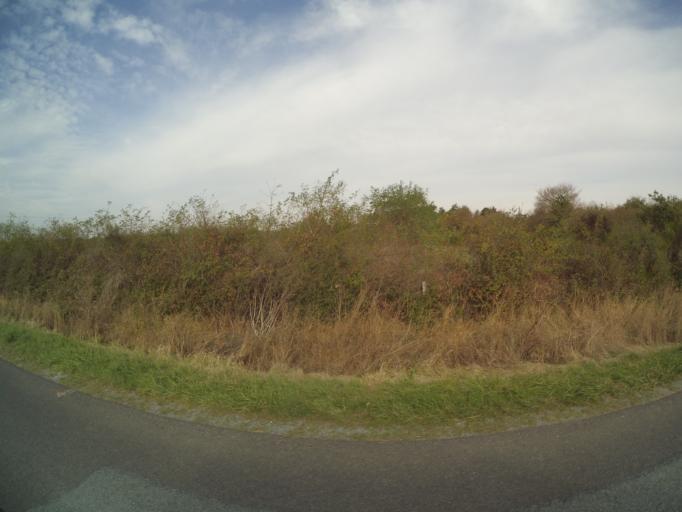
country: FR
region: Pays de la Loire
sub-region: Departement de Maine-et-Loire
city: Vihiers
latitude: 47.2085
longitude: -0.5288
